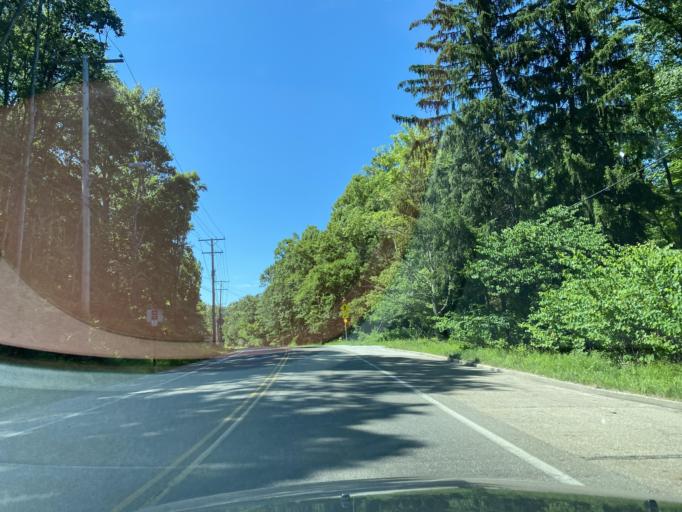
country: US
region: Ohio
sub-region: Summit County
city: Akron
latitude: 41.1301
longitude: -81.5422
